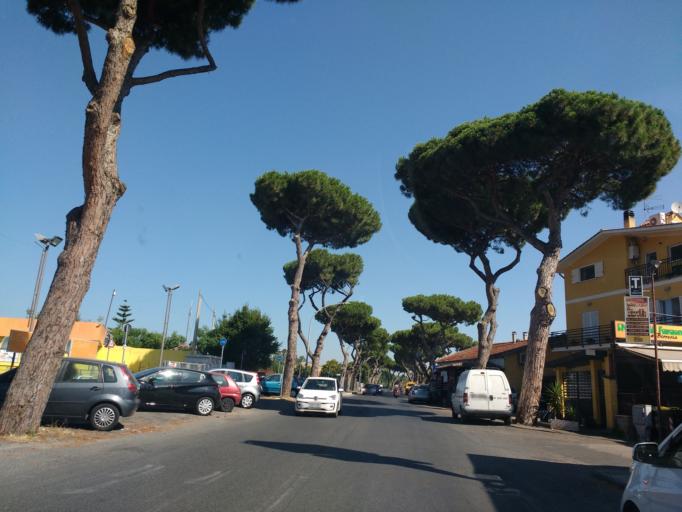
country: IT
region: Latium
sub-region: Citta metropolitana di Roma Capitale
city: Acilia-Castel Fusano-Ostia Antica
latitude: 41.7540
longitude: 12.3078
